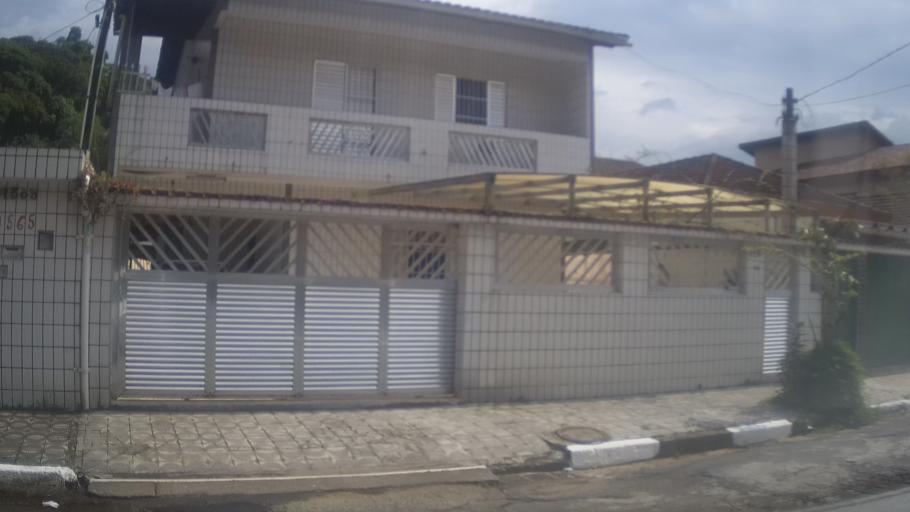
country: BR
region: Sao Paulo
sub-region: Santos
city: Santos
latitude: -23.9498
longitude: -46.3594
